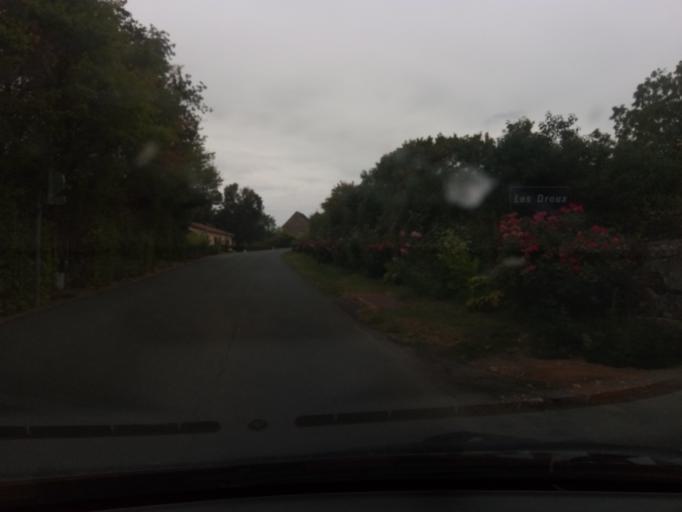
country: FR
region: Centre
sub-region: Departement de l'Indre
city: Tournon-Saint-Martin
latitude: 46.6909
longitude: 0.8823
